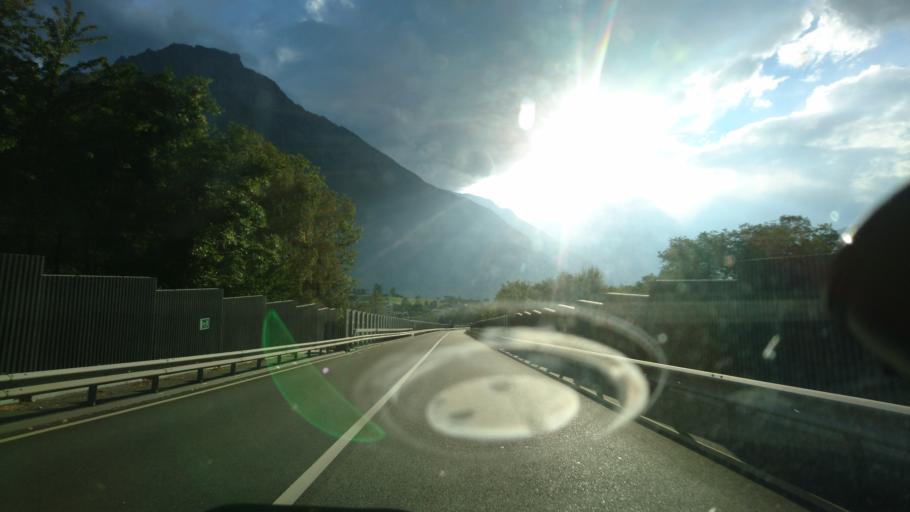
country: CH
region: Valais
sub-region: Brig District
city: Naters
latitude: 46.3183
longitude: 8.0169
